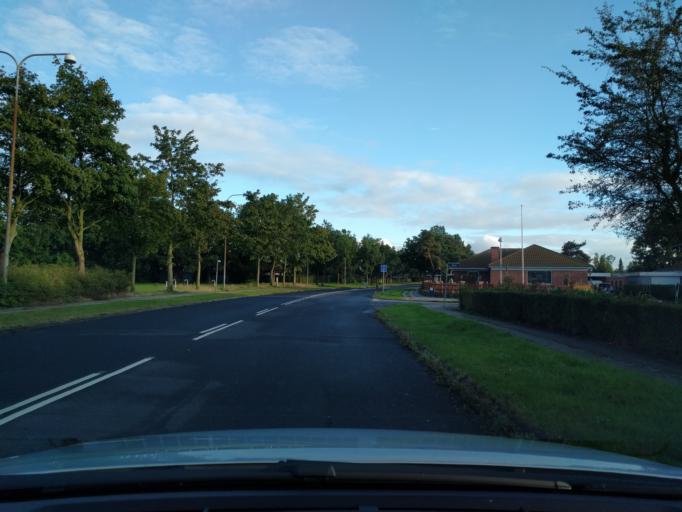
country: DK
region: South Denmark
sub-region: Odense Kommune
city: Bullerup
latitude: 55.4270
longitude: 10.4769
